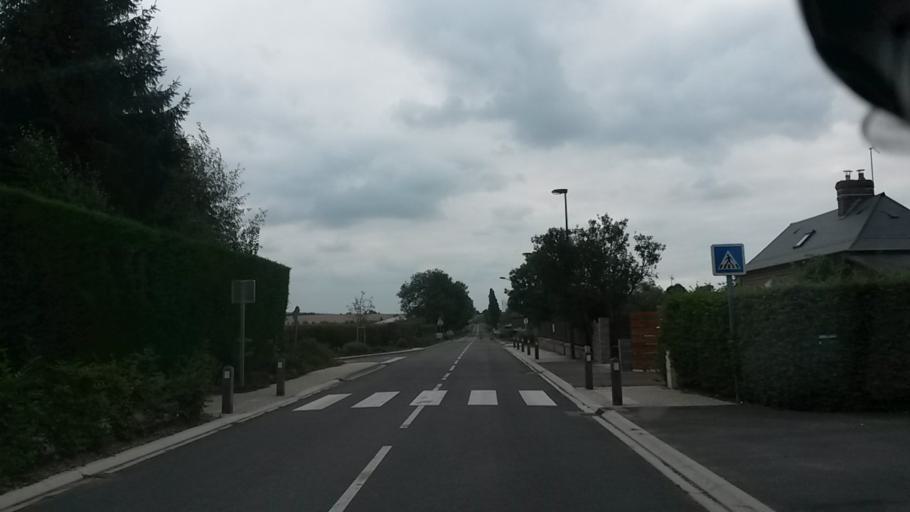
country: FR
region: Haute-Normandie
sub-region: Departement de la Seine-Maritime
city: Forges-les-Eaux
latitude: 49.5697
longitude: 1.5340
